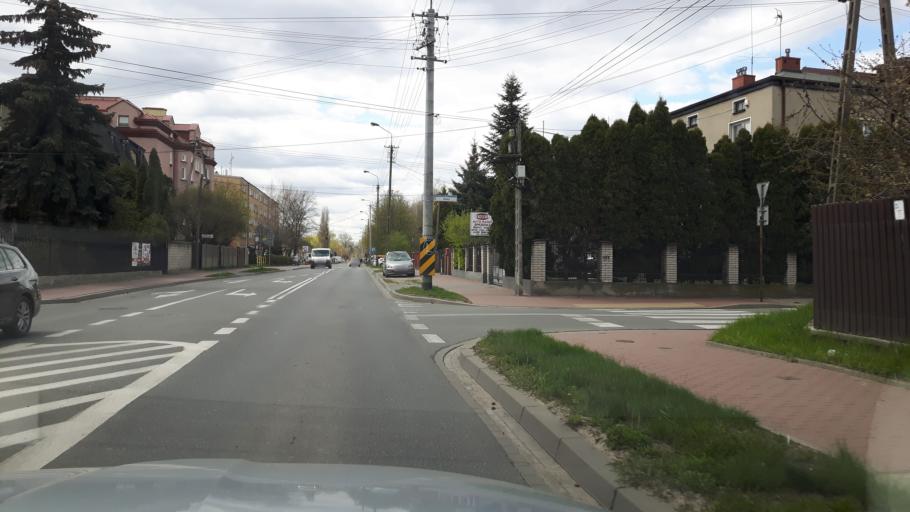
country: PL
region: Masovian Voivodeship
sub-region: Powiat wolominski
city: Wolomin
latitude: 52.3510
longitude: 21.2452
